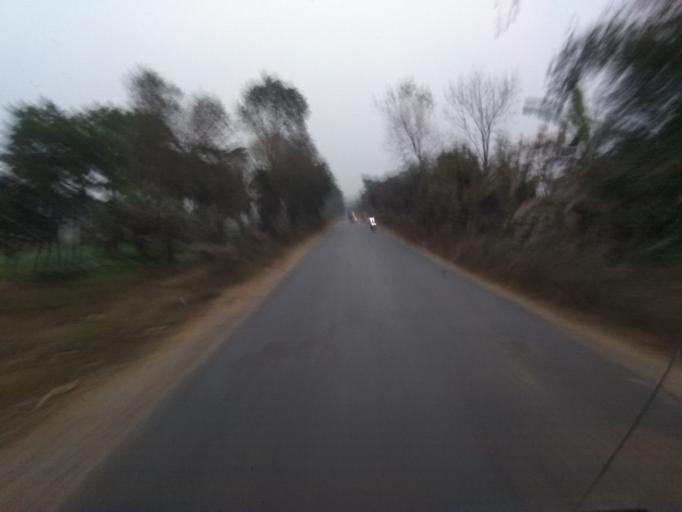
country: BD
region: Rajshahi
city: Bogra
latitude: 24.7467
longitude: 89.3390
